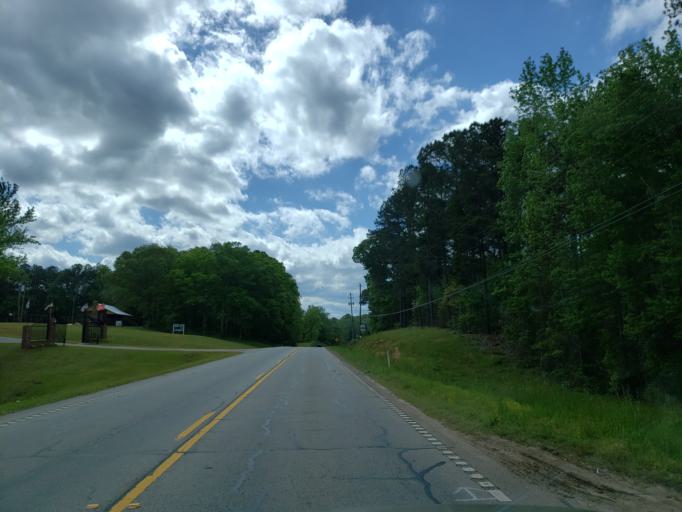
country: US
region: Georgia
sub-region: Haralson County
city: Tallapoosa
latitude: 33.7388
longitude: -85.2648
